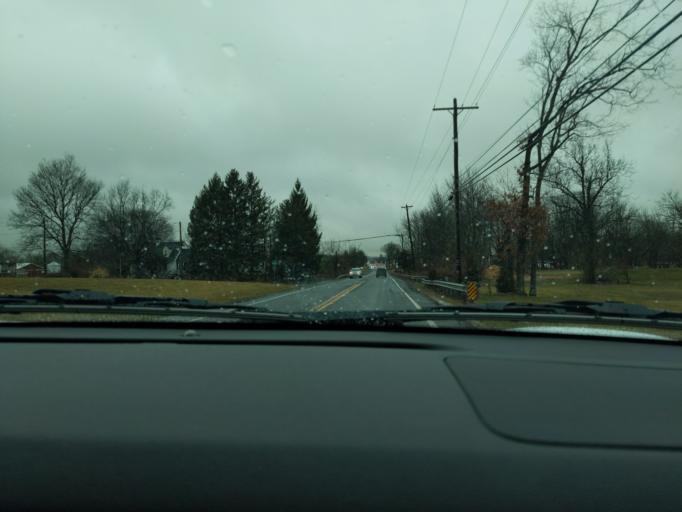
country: US
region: Pennsylvania
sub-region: Bucks County
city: Dublin
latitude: 40.3776
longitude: -75.2123
